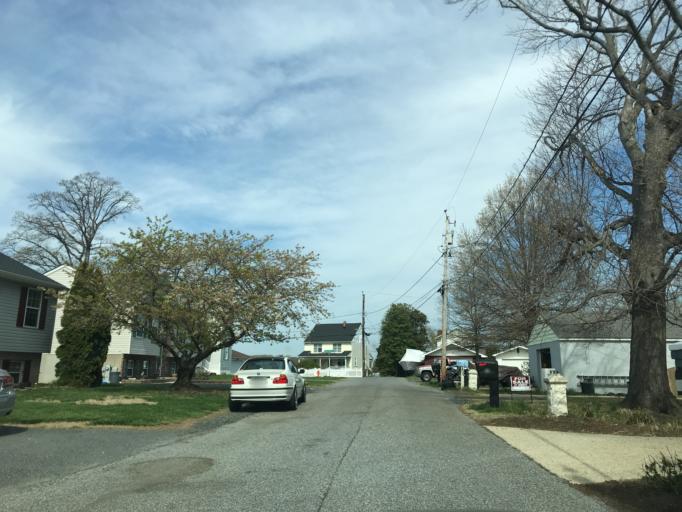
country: US
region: Maryland
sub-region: Baltimore County
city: Middle River
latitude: 39.3122
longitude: -76.4255
